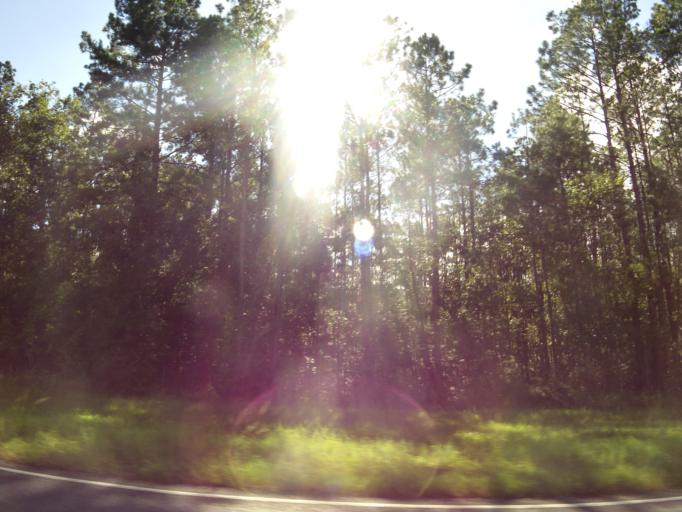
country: US
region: Georgia
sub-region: Camden County
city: Woodbine
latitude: 30.9003
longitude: -81.7100
